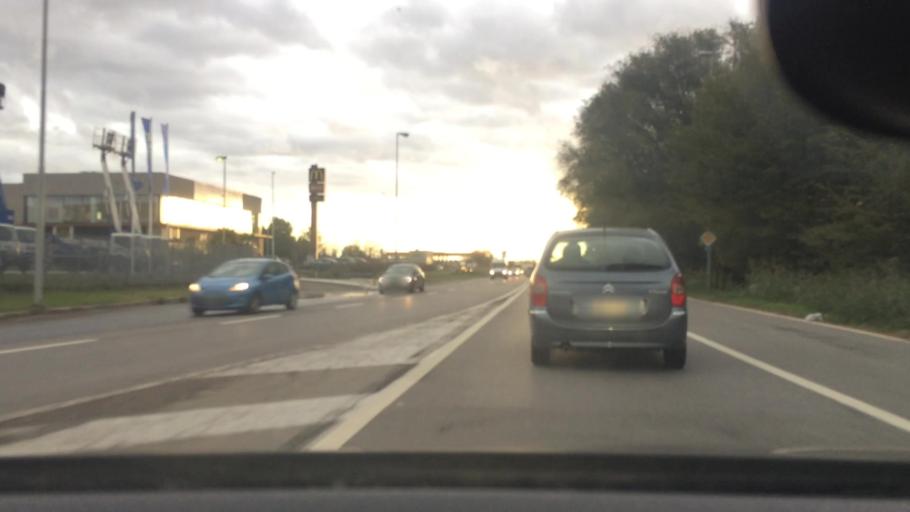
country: IT
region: Lombardy
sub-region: Citta metropolitana di Milano
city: Pogliano Milanese
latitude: 45.5411
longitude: 9.0161
